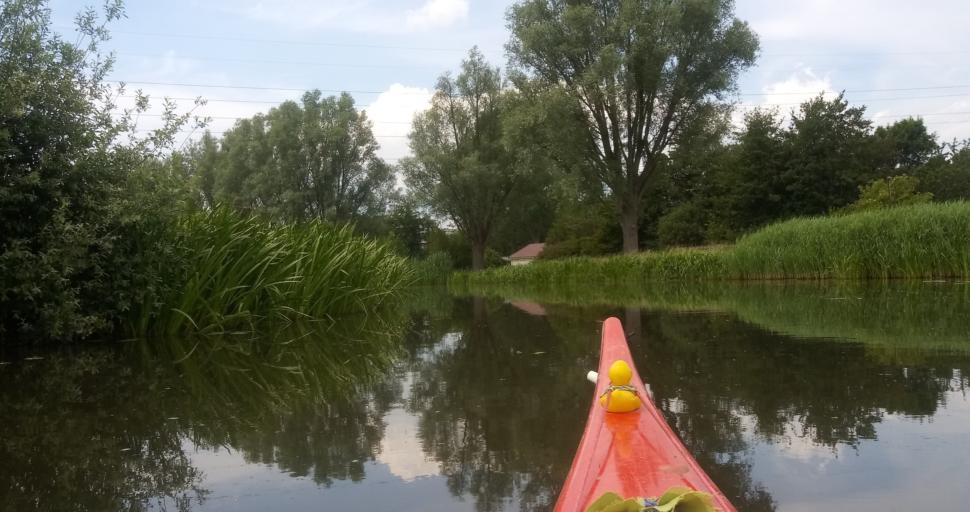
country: NL
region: Gelderland
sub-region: Gemeente Zutphen
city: Warnsveld
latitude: 52.1469
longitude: 6.2210
